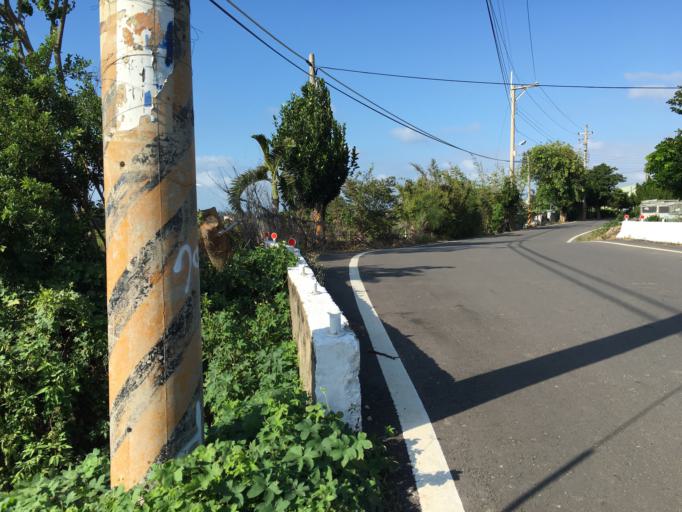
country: TW
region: Taiwan
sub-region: Hsinchu
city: Zhubei
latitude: 24.9262
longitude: 120.9844
